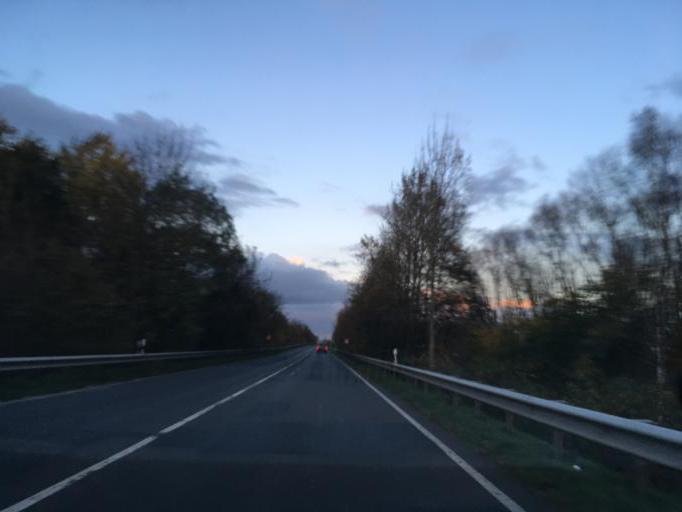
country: DE
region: Lower Saxony
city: Winsen
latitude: 53.3591
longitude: 10.1697
